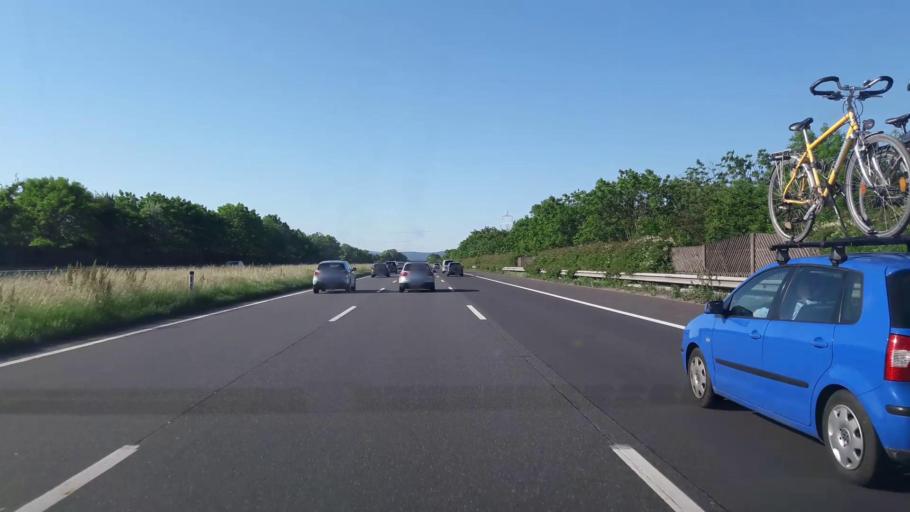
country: AT
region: Lower Austria
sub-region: Politischer Bezirk Baden
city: Leobersdorf
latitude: 47.8944
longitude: 16.2072
